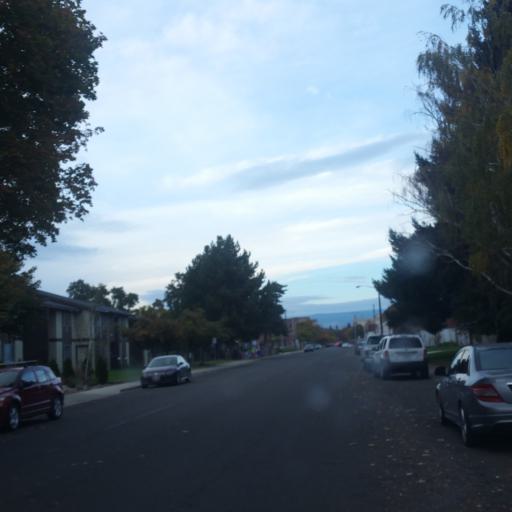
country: US
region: Washington
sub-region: Kittitas County
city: Ellensburg
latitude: 46.9914
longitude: -120.5471
